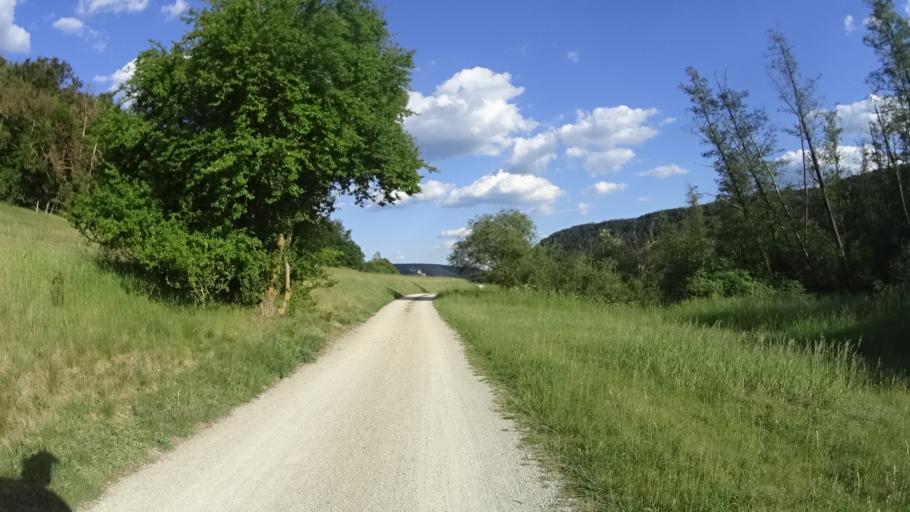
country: DE
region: Bavaria
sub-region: Upper Palatinate
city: Dietfurt
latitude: 49.0189
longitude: 11.6031
